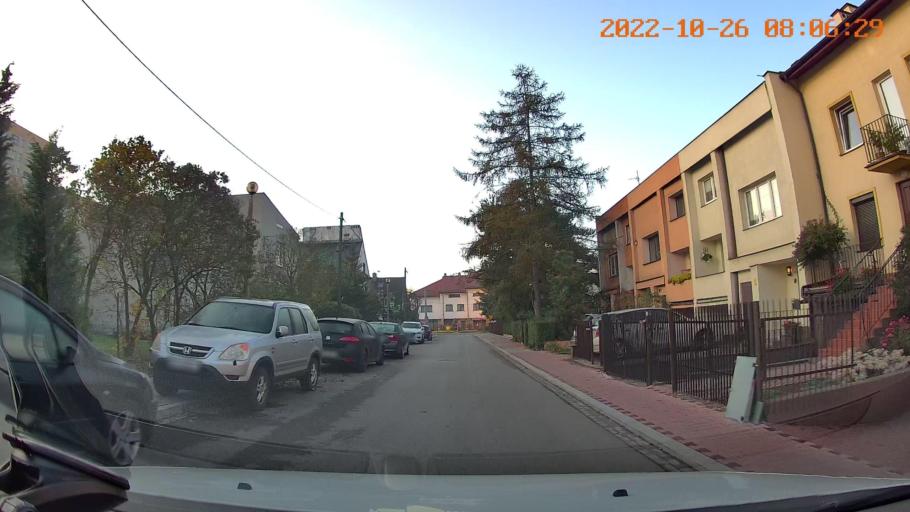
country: PL
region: Lesser Poland Voivodeship
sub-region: Krakow
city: Krakow
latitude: 50.0870
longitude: 19.9146
